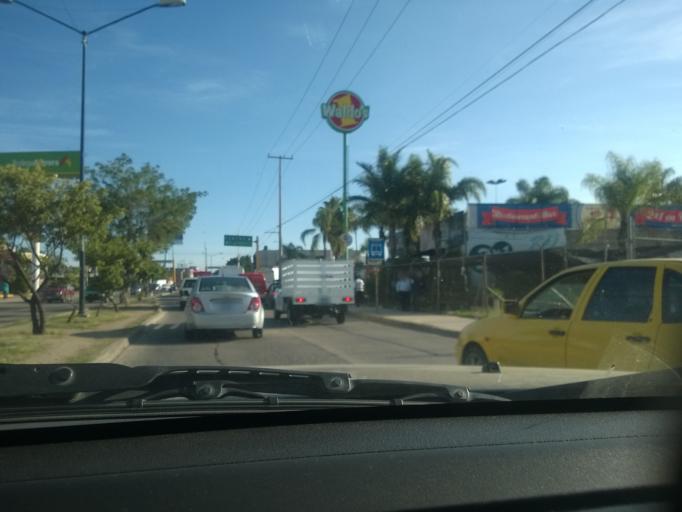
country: MX
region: Guanajuato
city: Leon
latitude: 21.1320
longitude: -101.6598
